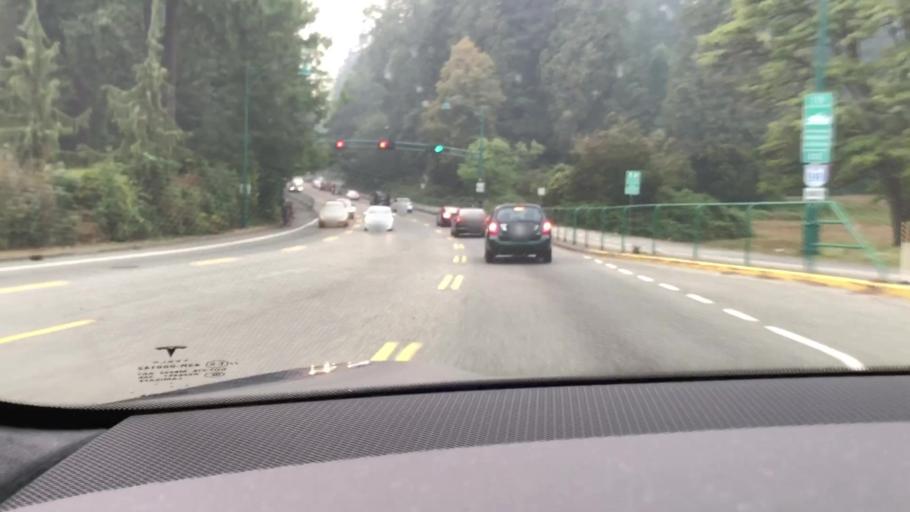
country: CA
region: British Columbia
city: West End
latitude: 49.2977
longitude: -123.1371
